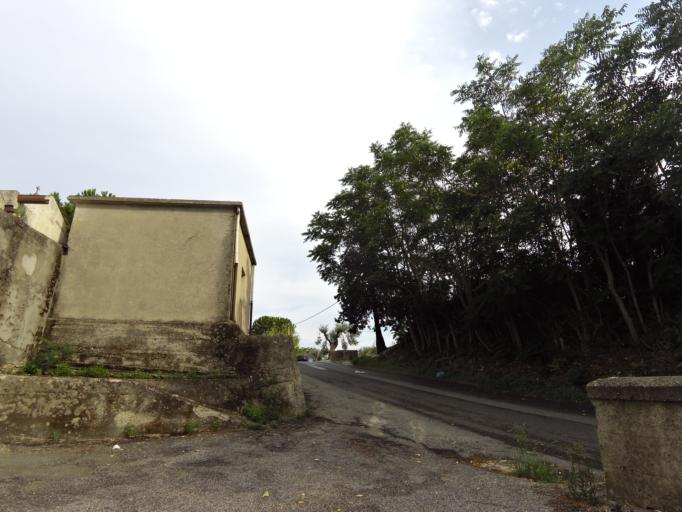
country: IT
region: Calabria
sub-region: Provincia di Reggio Calabria
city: Stignano
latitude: 38.4223
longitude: 16.4667
